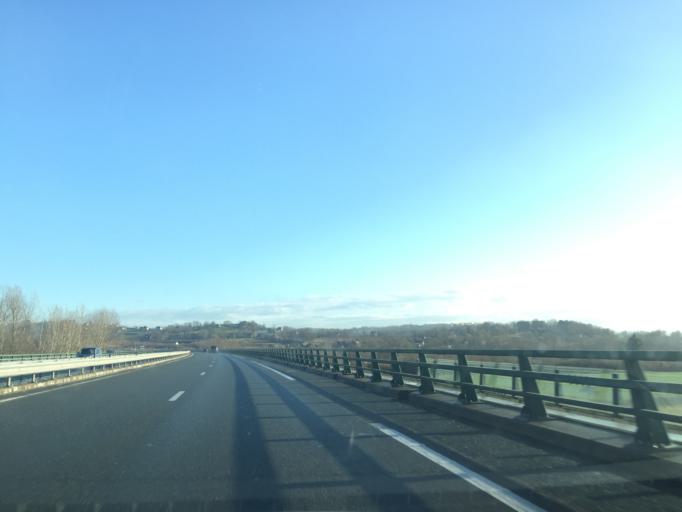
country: FR
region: Limousin
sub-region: Departement de la Correze
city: Saint-Pantaleon-de-Larche
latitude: 45.1657
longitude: 1.4600
